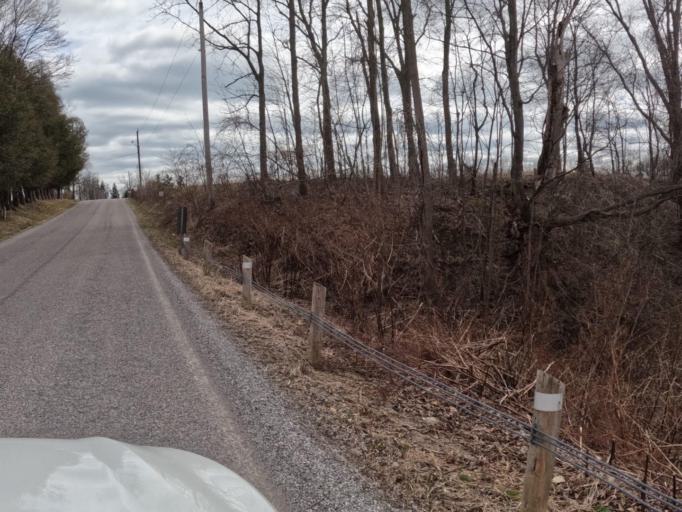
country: CA
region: Ontario
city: Norfolk County
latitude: 42.8047
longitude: -80.2150
